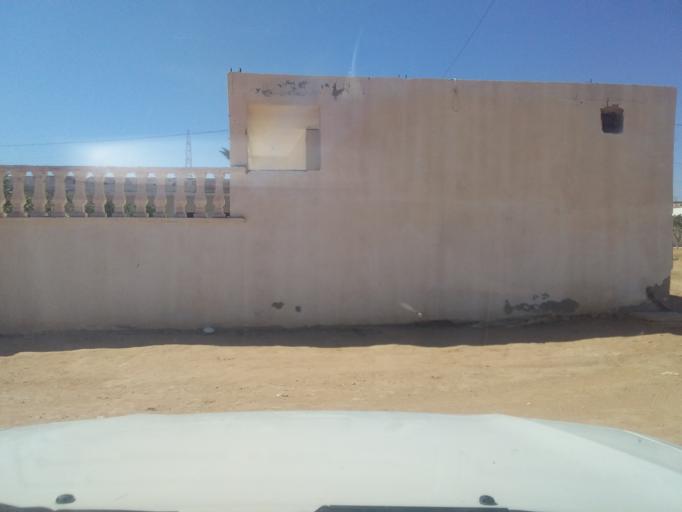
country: TN
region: Qabis
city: Matmata
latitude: 33.5802
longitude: 10.2813
